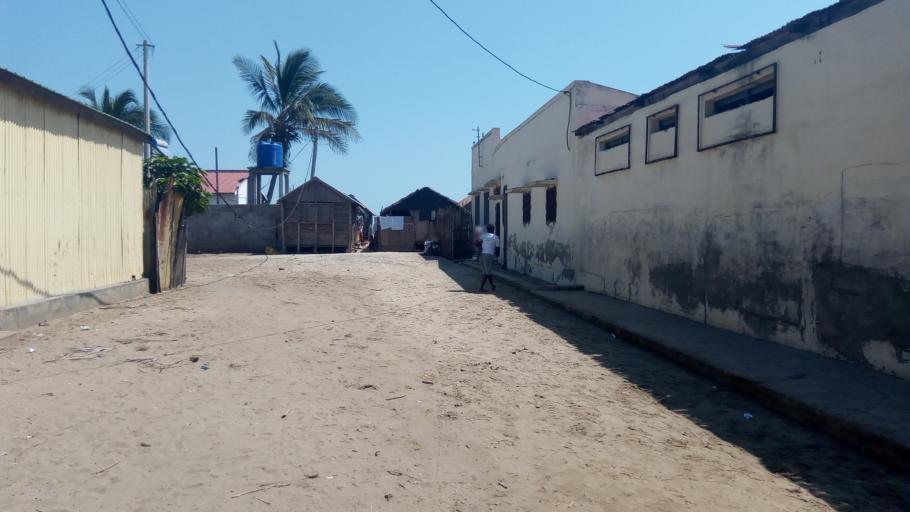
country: MG
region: Menabe
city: Morondava
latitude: -20.2914
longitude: 44.2732
